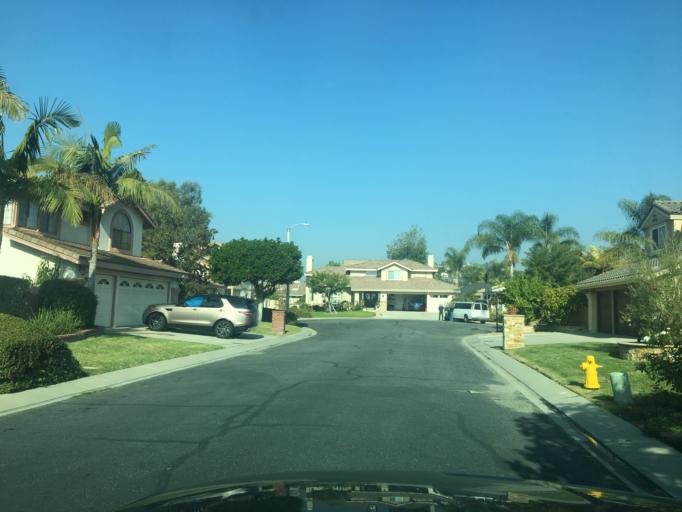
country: US
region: California
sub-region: Orange County
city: North Tustin
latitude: 33.7666
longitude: -117.8021
